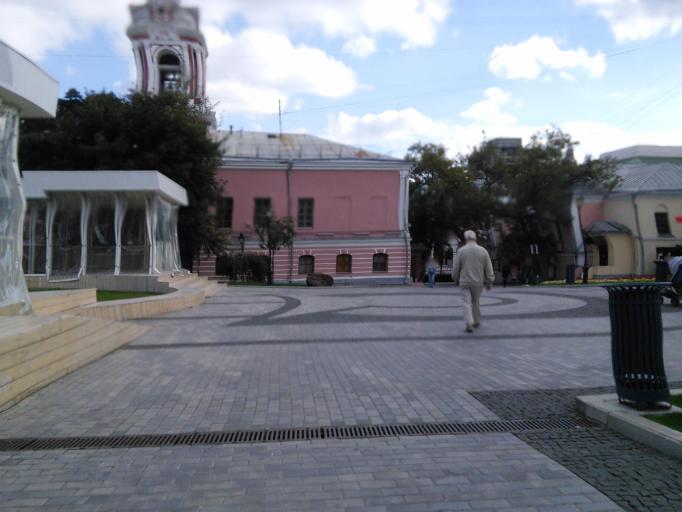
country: RU
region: Moscow
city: Taganskiy
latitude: 55.7662
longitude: 37.6605
